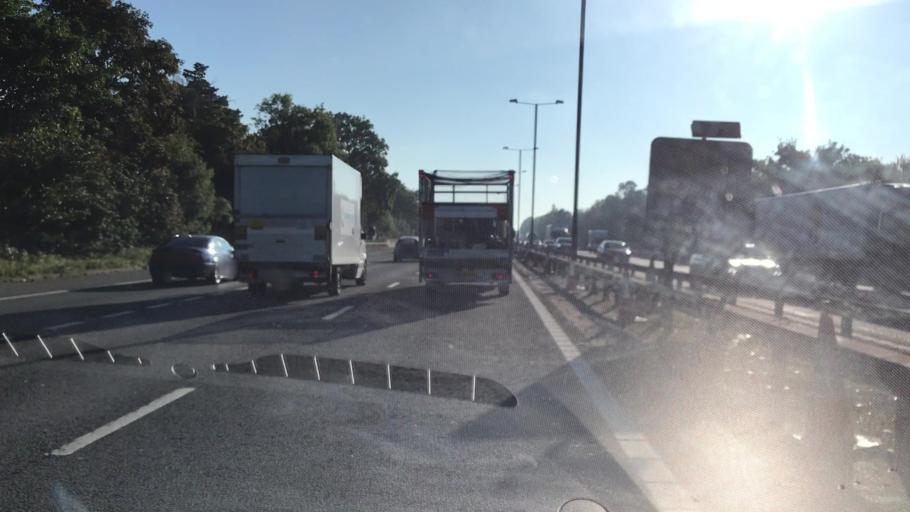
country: GB
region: England
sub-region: Greater London
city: Hayes
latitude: 51.4936
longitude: -0.4278
